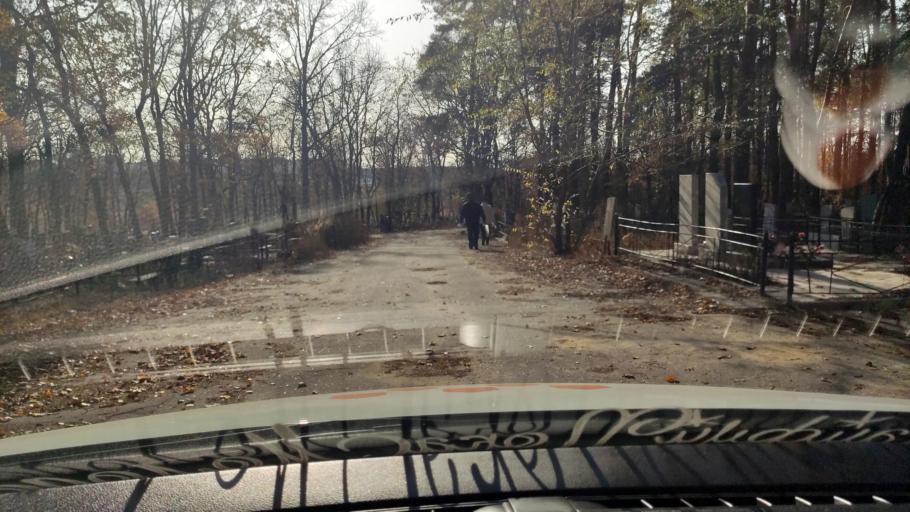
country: RU
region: Voronezj
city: Pridonskoy
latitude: 51.6678
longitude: 39.0968
